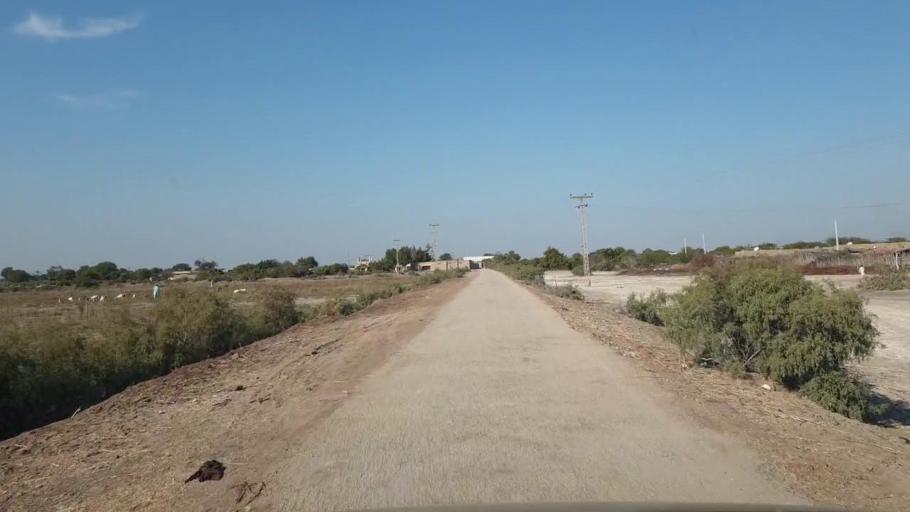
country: PK
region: Sindh
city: Shahpur Chakar
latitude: 26.1535
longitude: 68.6839
